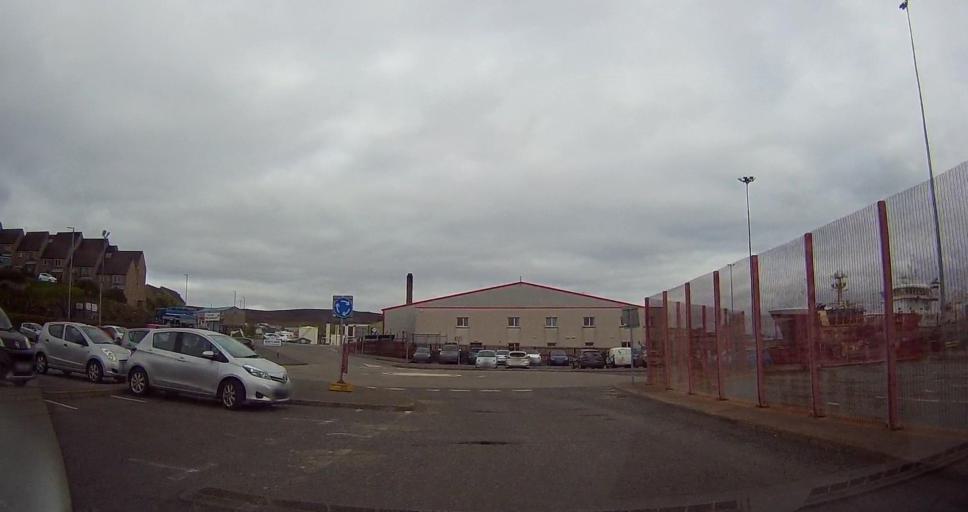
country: GB
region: Scotland
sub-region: Shetland Islands
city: Lerwick
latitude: 60.1630
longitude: -1.1583
